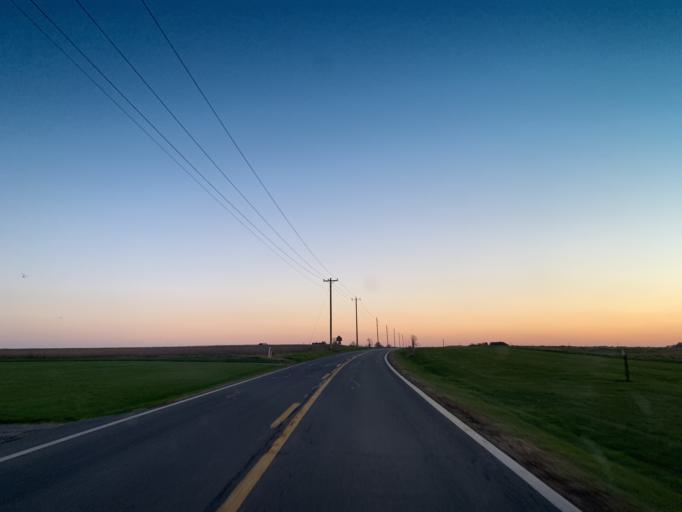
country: US
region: Delaware
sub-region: New Castle County
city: Middletown
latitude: 39.4213
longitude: -75.7419
